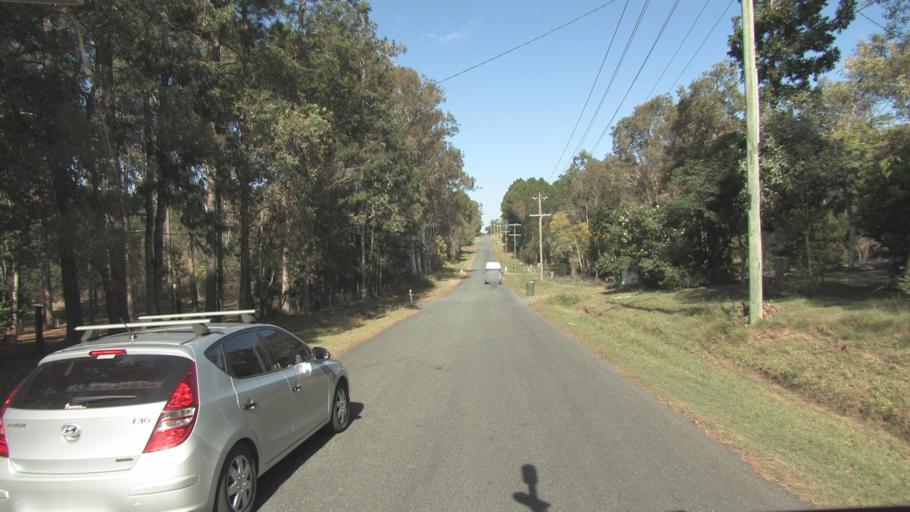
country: AU
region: Queensland
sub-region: Logan
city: North Maclean
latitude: -27.7737
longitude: 152.9917
